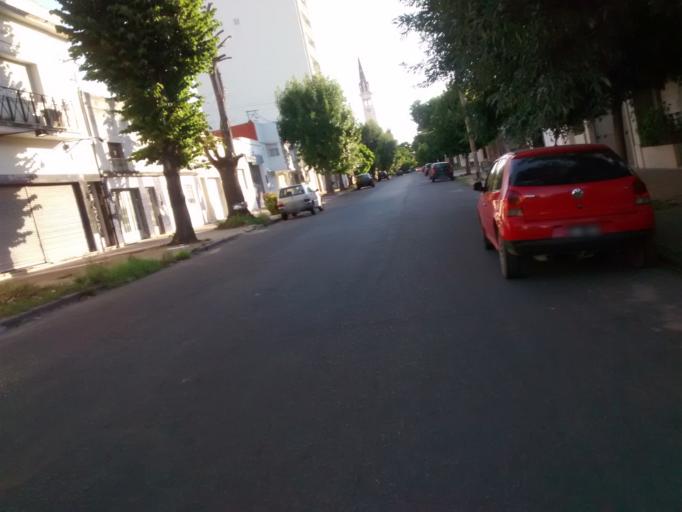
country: AR
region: Buenos Aires
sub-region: Partido de La Plata
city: La Plata
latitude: -34.9216
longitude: -57.9341
